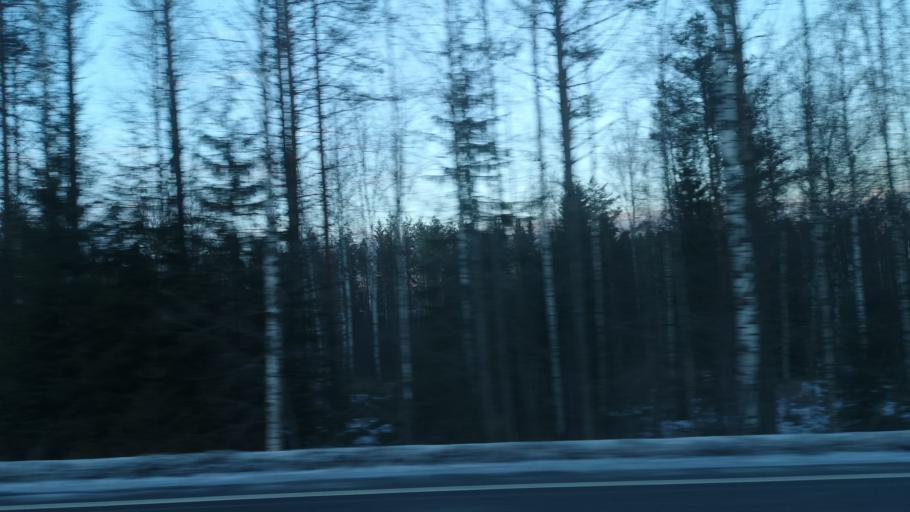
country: FI
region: Southern Savonia
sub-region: Savonlinna
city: Sulkava
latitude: 61.9560
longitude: 28.4654
